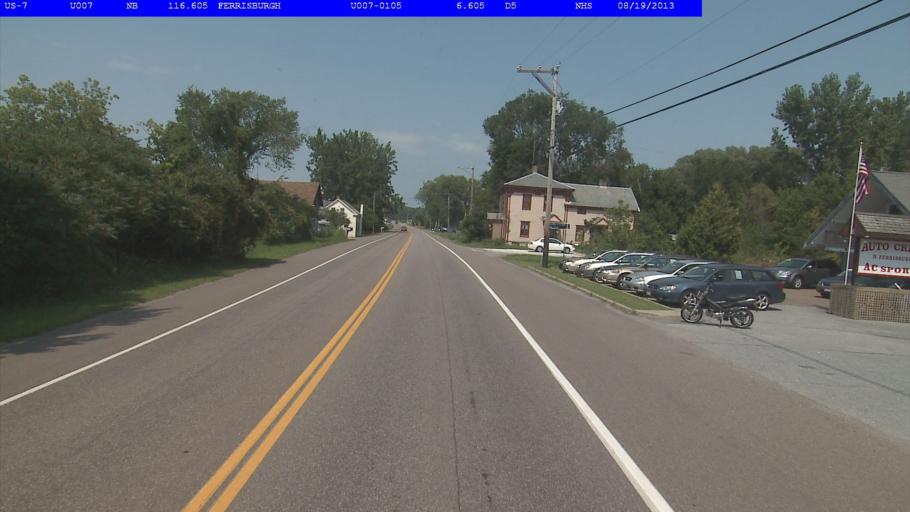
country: US
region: Vermont
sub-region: Addison County
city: Vergennes
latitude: 44.2530
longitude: -73.2275
